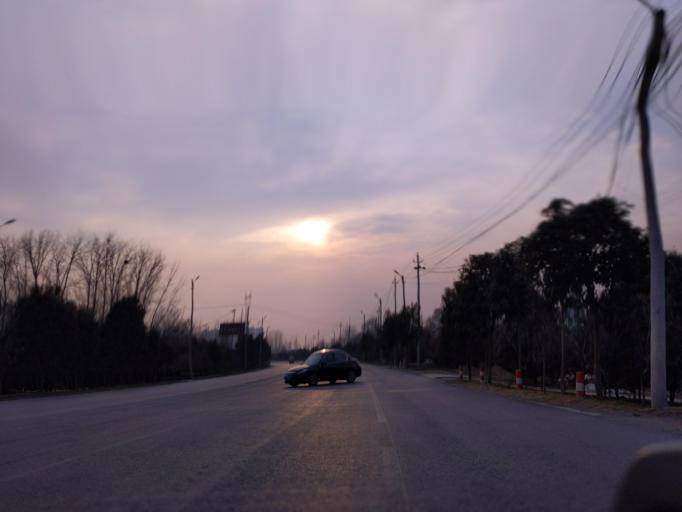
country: CN
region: Henan Sheng
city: Puyang
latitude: 35.8199
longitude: 114.9757
